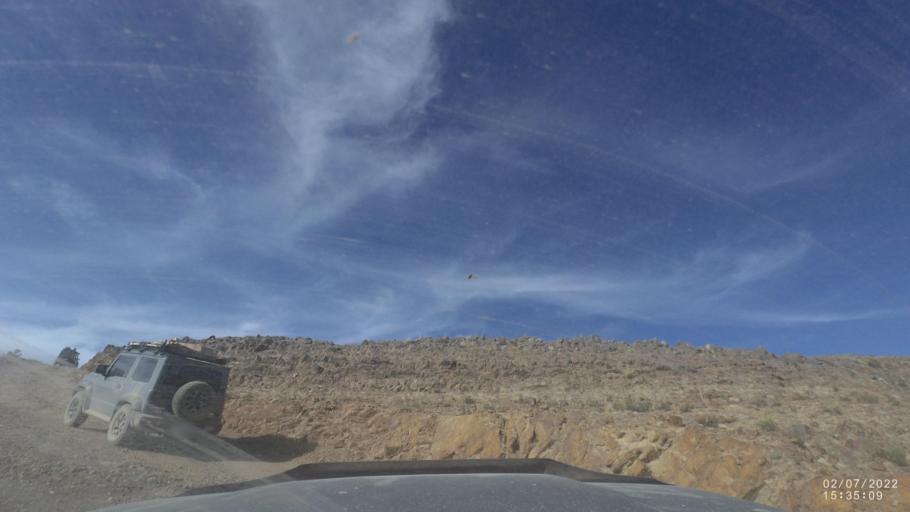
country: BO
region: Cochabamba
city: Irpa Irpa
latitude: -17.8886
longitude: -66.4115
